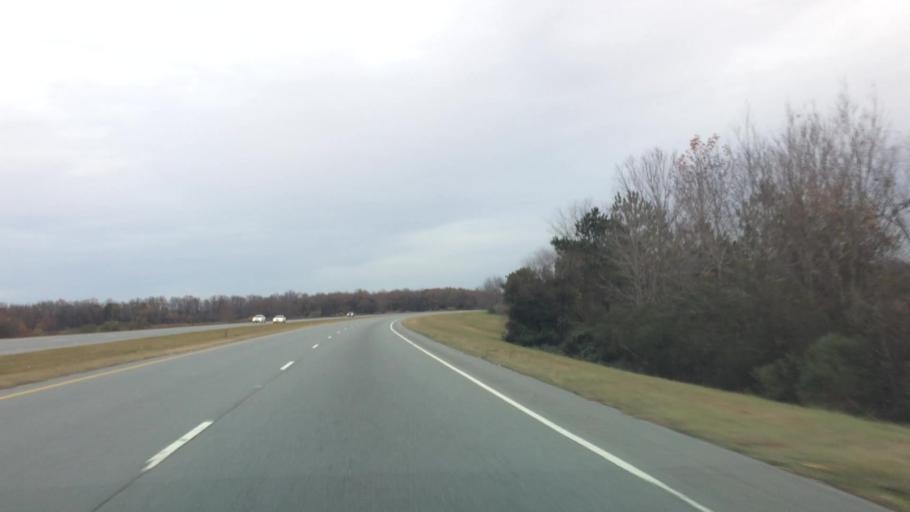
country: US
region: North Carolina
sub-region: Wayne County
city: Mount Olive
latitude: 35.1227
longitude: -78.1758
